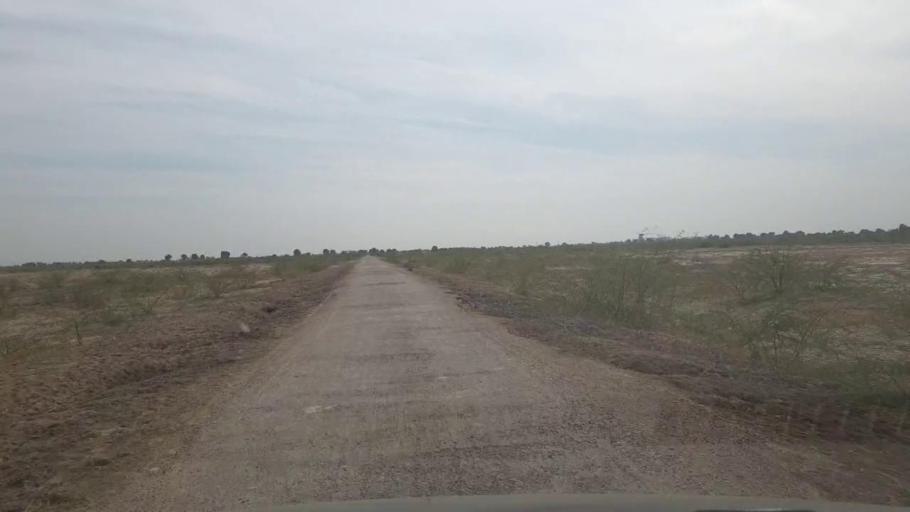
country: PK
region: Sindh
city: Kunri
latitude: 25.2441
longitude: 69.6064
